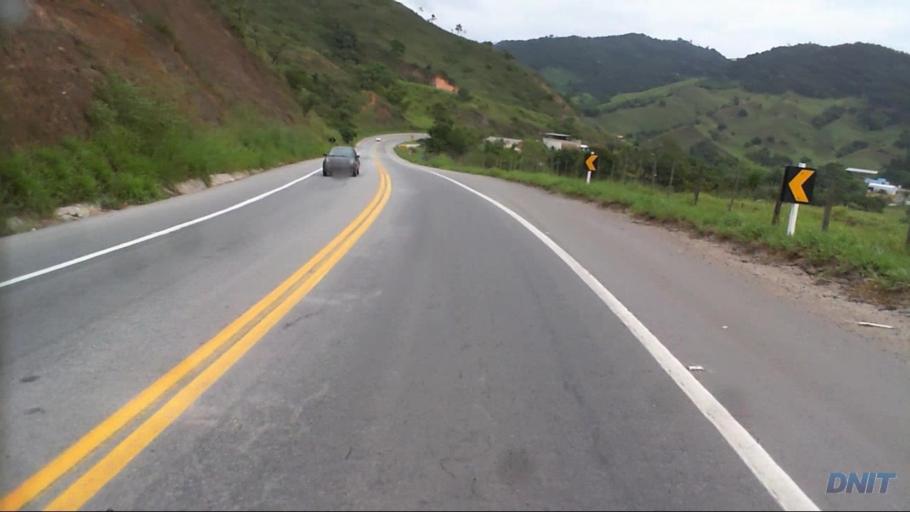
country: BR
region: Minas Gerais
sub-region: Timoteo
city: Timoteo
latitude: -19.6200
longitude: -42.8424
